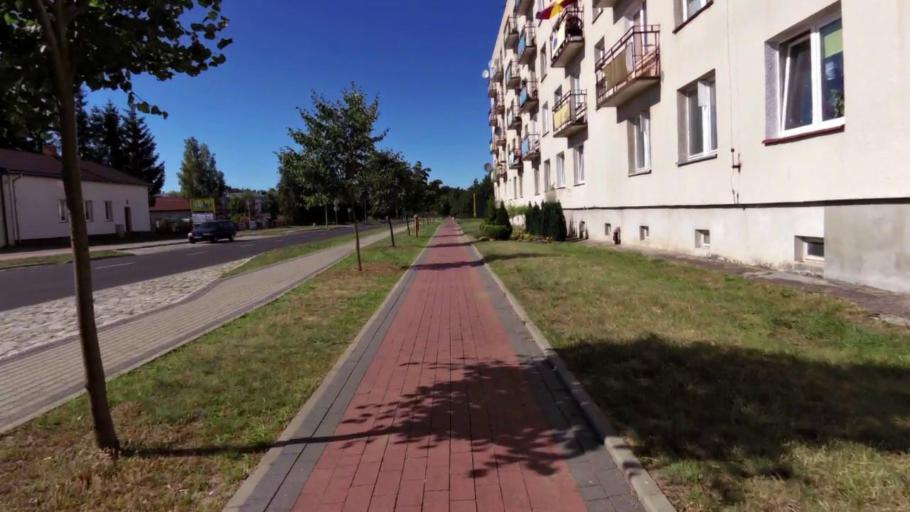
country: PL
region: West Pomeranian Voivodeship
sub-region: Powiat szczecinecki
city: Borne Sulinowo
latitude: 53.5771
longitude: 16.5512
